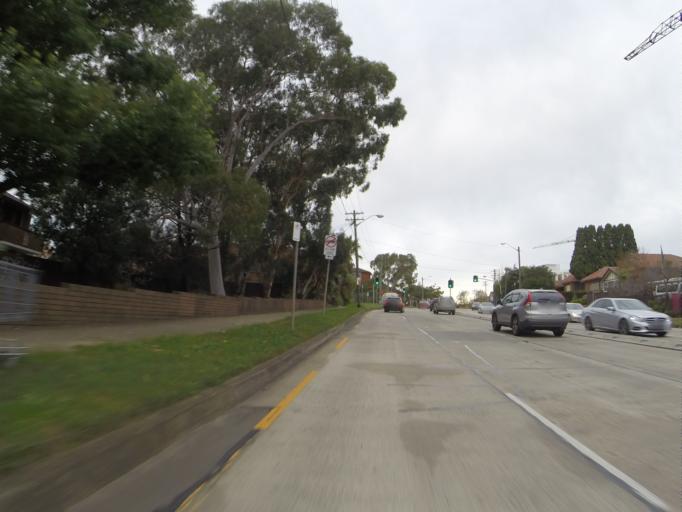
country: AU
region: New South Wales
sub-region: Strathfield
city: Strathfield South
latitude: -33.8894
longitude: 151.0781
